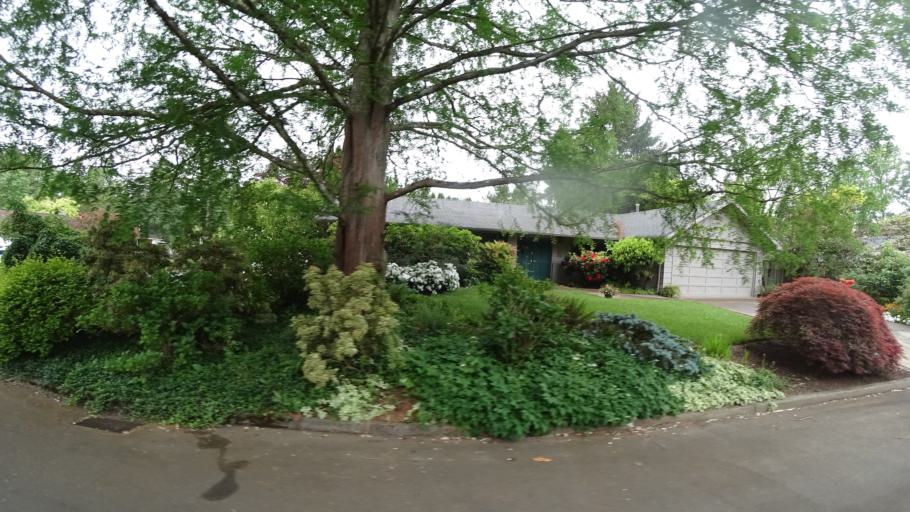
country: US
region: Oregon
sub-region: Washington County
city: Garden Home-Whitford
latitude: 45.4699
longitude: -122.7669
